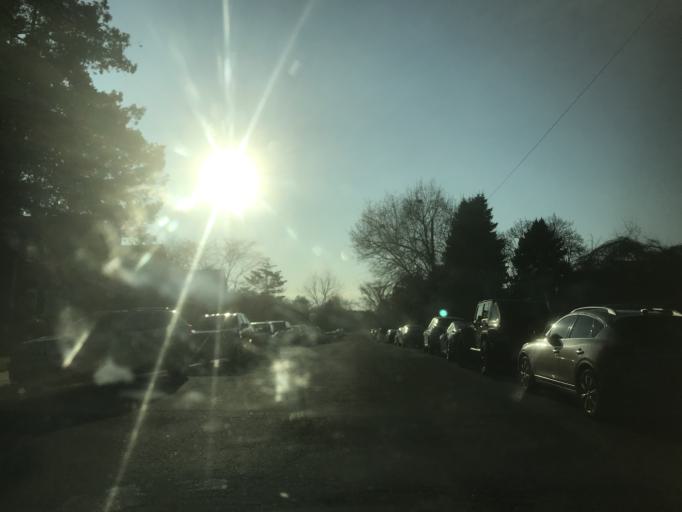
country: US
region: Maryland
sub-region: Baltimore County
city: Towson
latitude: 39.3905
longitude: -76.5722
